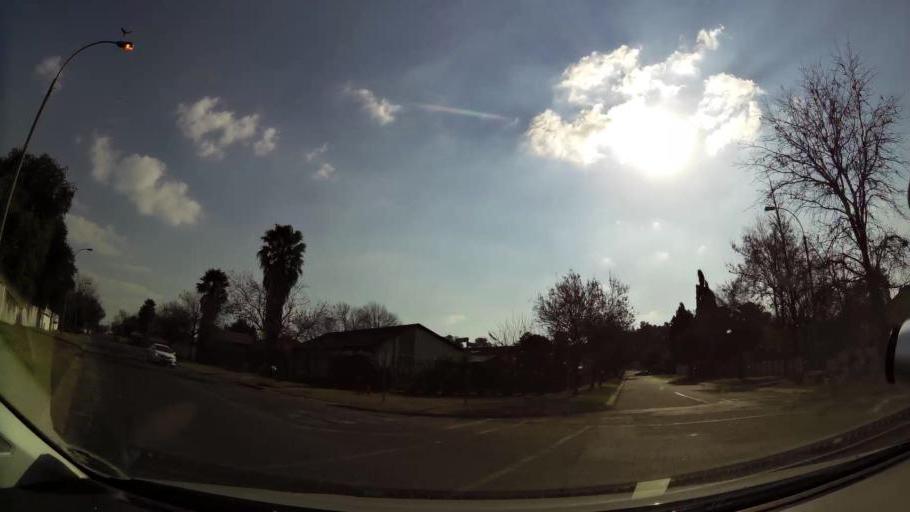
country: ZA
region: Gauteng
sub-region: City of Johannesburg Metropolitan Municipality
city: Modderfontein
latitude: -26.0863
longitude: 28.1977
